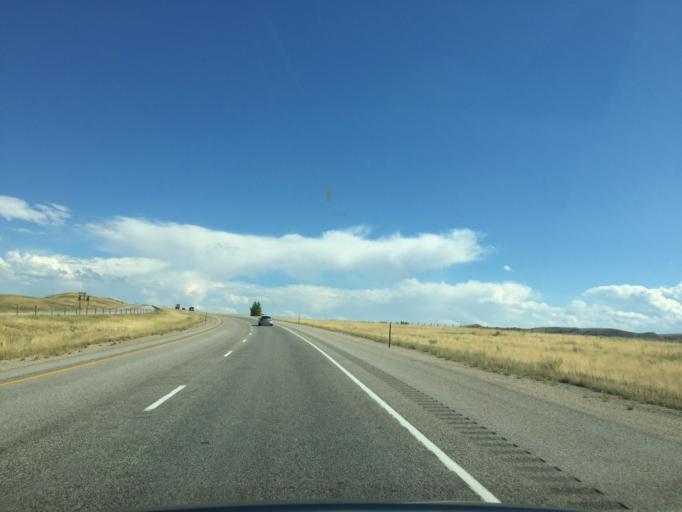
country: US
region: Wyoming
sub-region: Sheridan County
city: Sheridan
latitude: 44.6025
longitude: -106.8471
